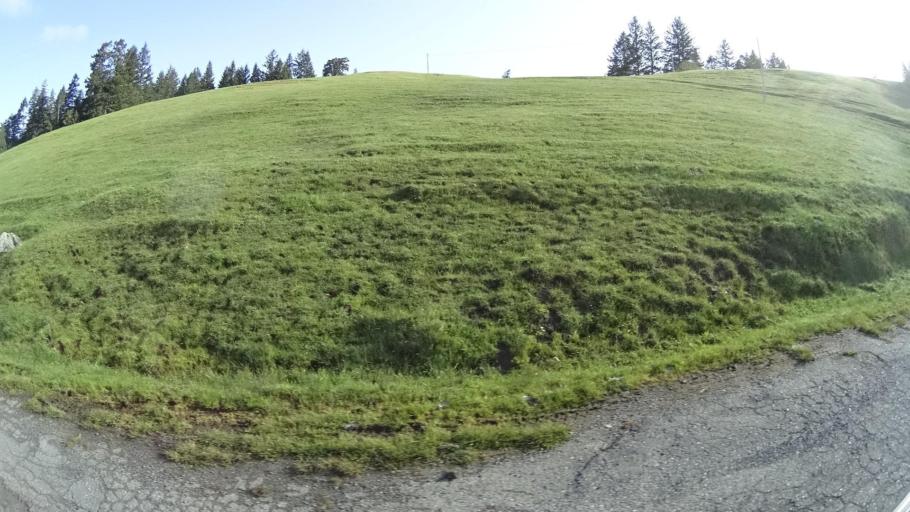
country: US
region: California
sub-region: Humboldt County
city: Bayside
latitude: 40.6903
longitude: -123.9390
